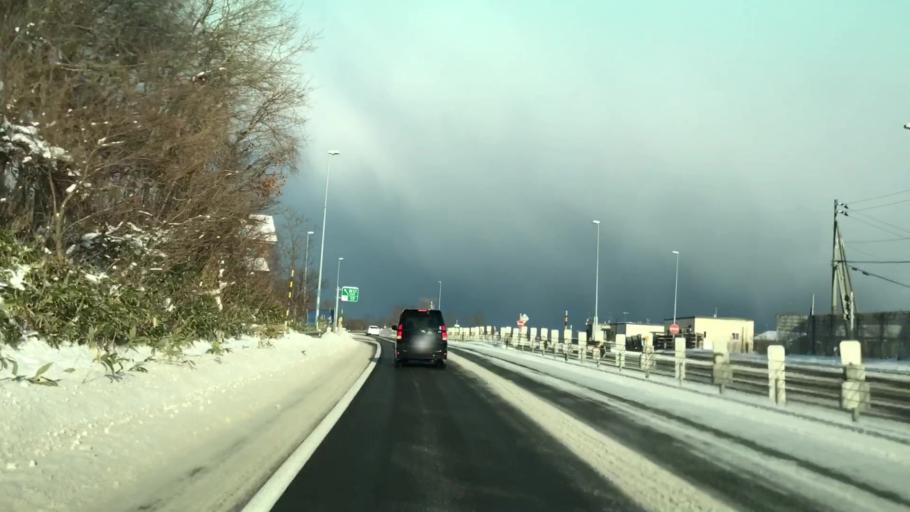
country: JP
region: Hokkaido
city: Sapporo
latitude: 43.1090
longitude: 141.2410
